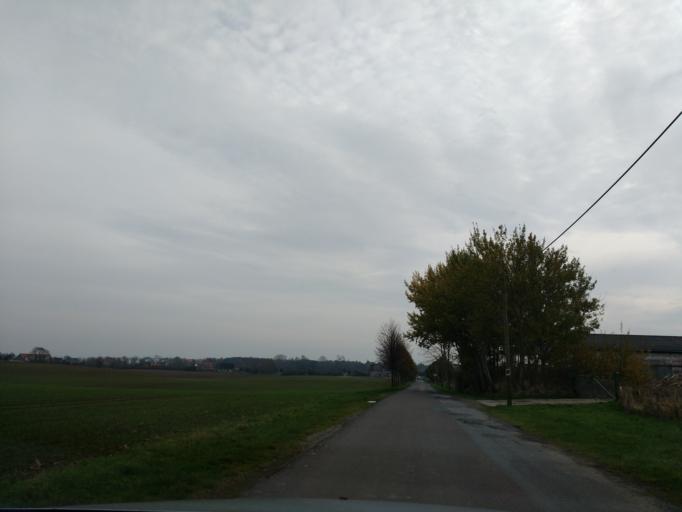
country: DE
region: Mecklenburg-Vorpommern
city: Ostseebad Boltenhagen
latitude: 53.9986
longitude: 11.1794
